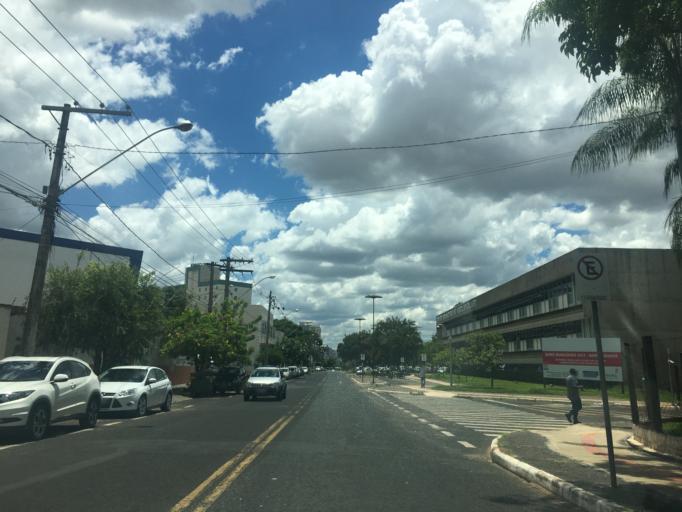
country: BR
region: Minas Gerais
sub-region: Uberlandia
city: Uberlandia
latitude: -18.9118
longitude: -48.2549
